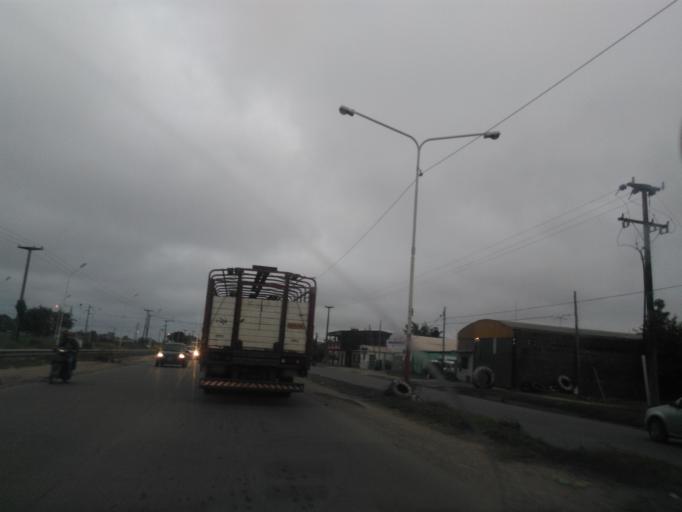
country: AR
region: Chaco
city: Resistencia
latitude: -27.4728
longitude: -59.0053
